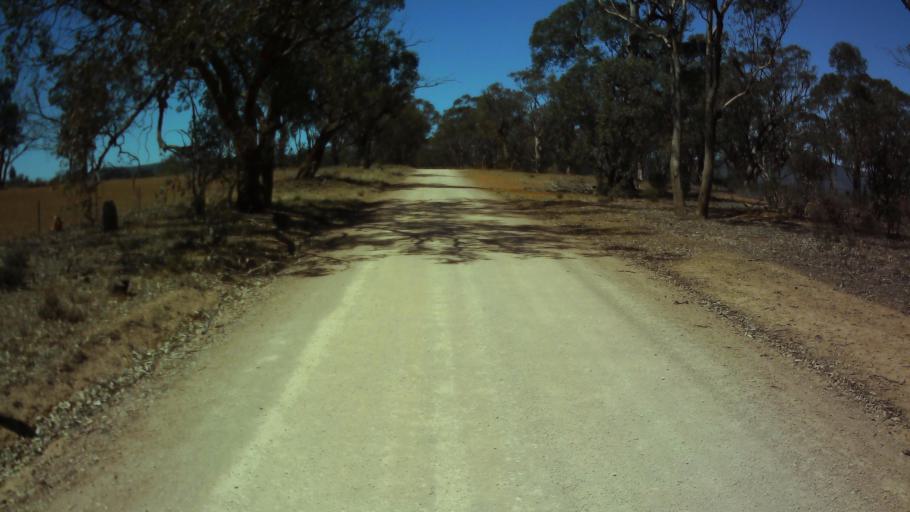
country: AU
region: New South Wales
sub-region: Weddin
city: Grenfell
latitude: -33.9308
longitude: 148.0776
